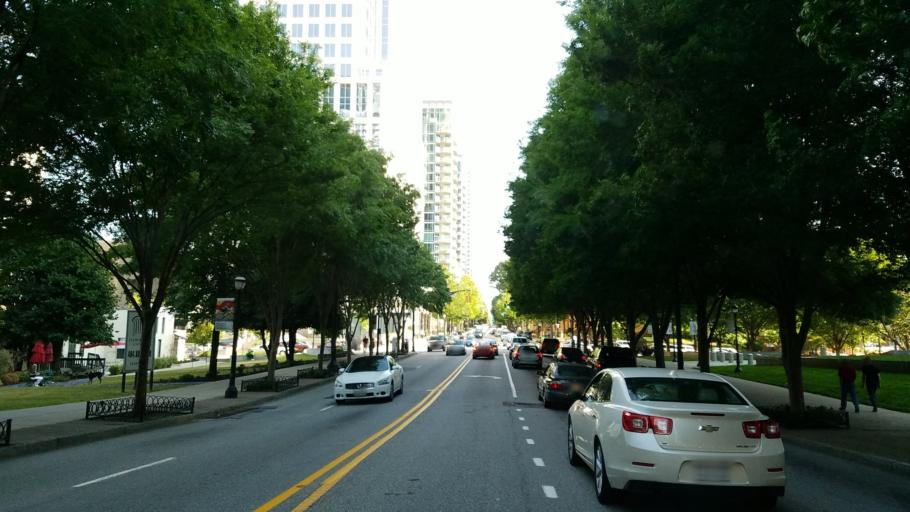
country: US
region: Georgia
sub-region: Fulton County
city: Atlanta
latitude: 33.7825
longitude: -84.3838
